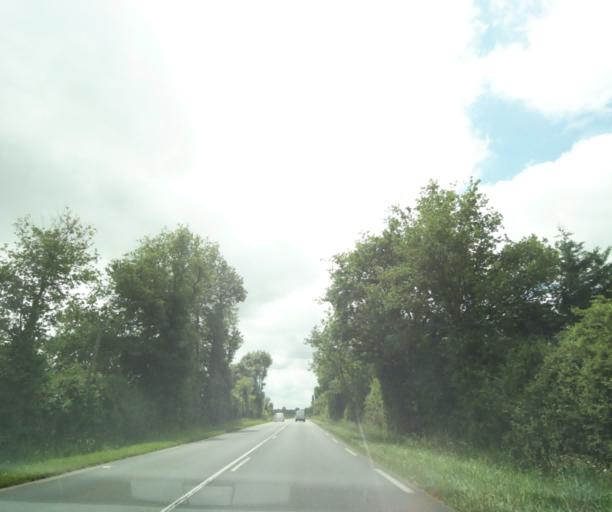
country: FR
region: Poitou-Charentes
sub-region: Departement des Deux-Sevres
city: Viennay
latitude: 46.7094
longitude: -0.2395
